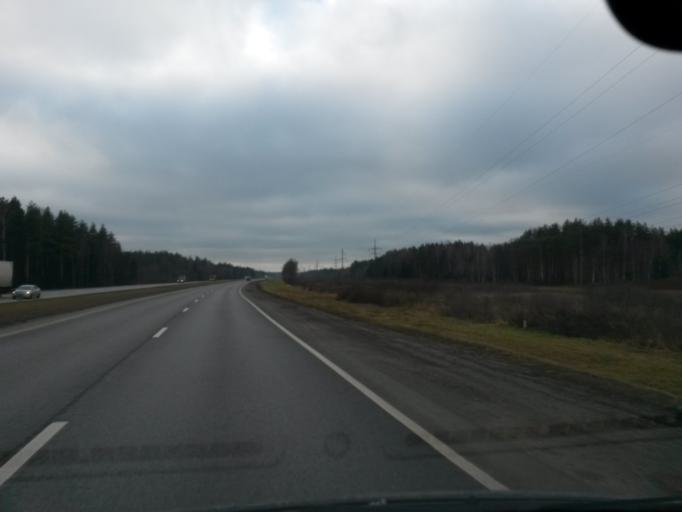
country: RU
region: Jaroslavl
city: Krasnyye Tkachi
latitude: 57.4902
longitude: 39.7810
